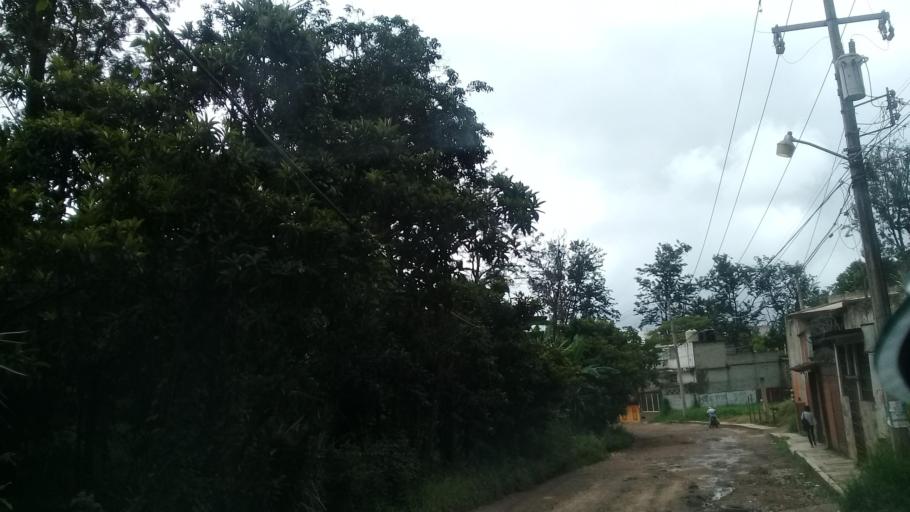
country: MX
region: Veracruz
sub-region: Xalapa
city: Colonia Santa Barbara
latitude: 19.4965
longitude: -96.8711
